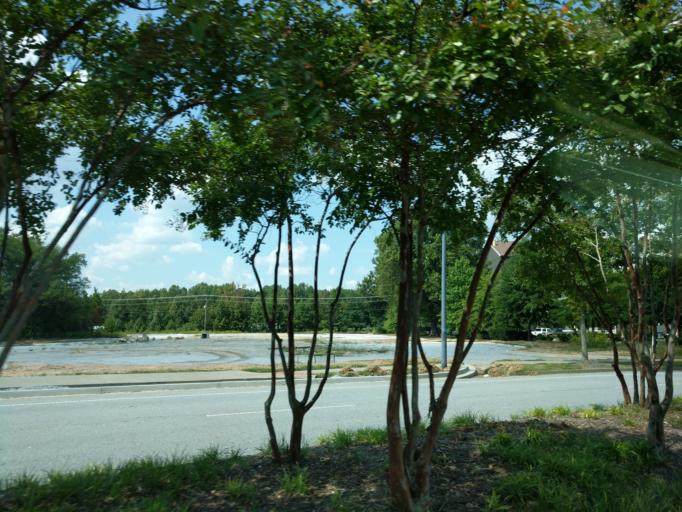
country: US
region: South Carolina
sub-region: Greenville County
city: Mauldin
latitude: 34.8241
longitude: -82.3074
